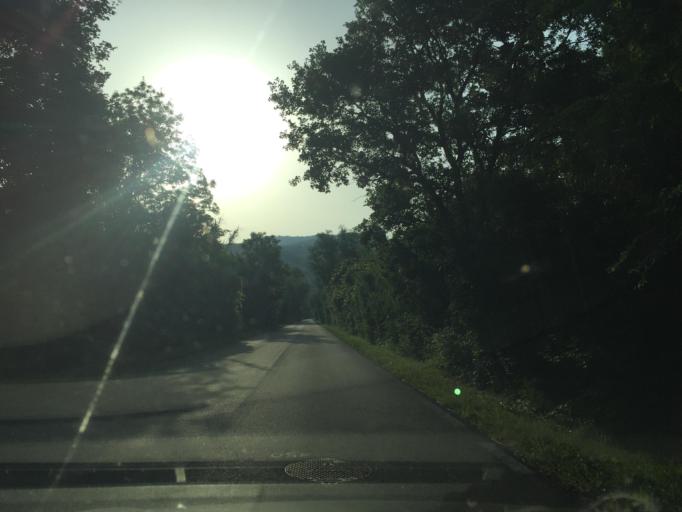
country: IT
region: Friuli Venezia Giulia
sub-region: Provincia di Trieste
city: Domio
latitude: 45.5881
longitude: 13.8232
